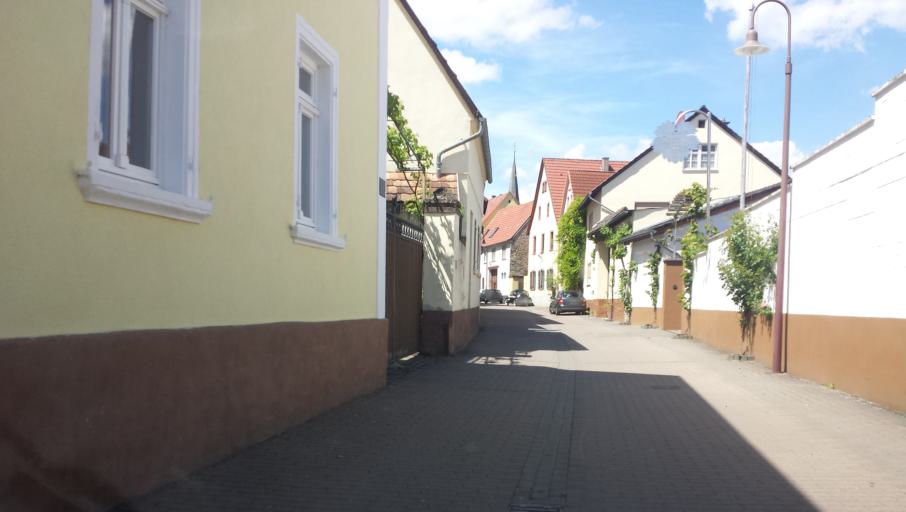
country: DE
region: Rheinland-Pfalz
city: Gundersheim
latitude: 49.6935
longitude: 8.2045
